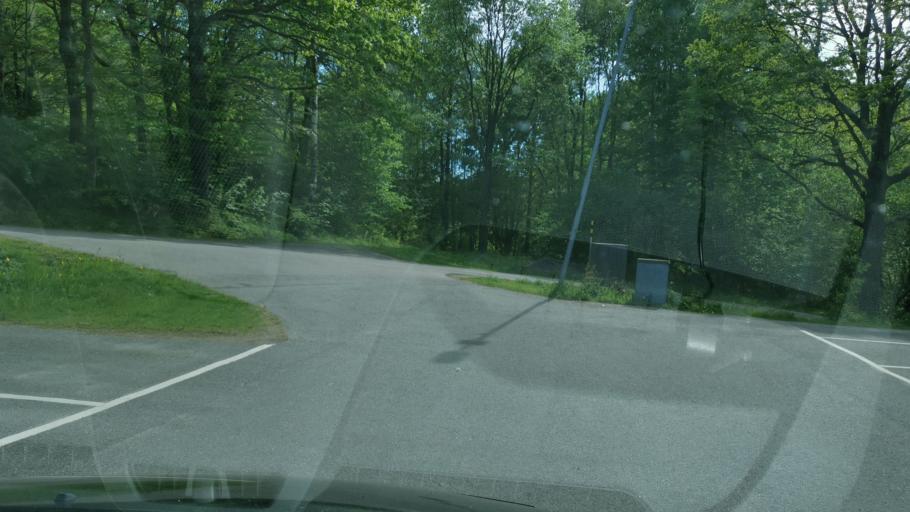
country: SE
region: Vaestra Goetaland
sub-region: Orust
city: Henan
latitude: 58.2634
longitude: 11.5973
